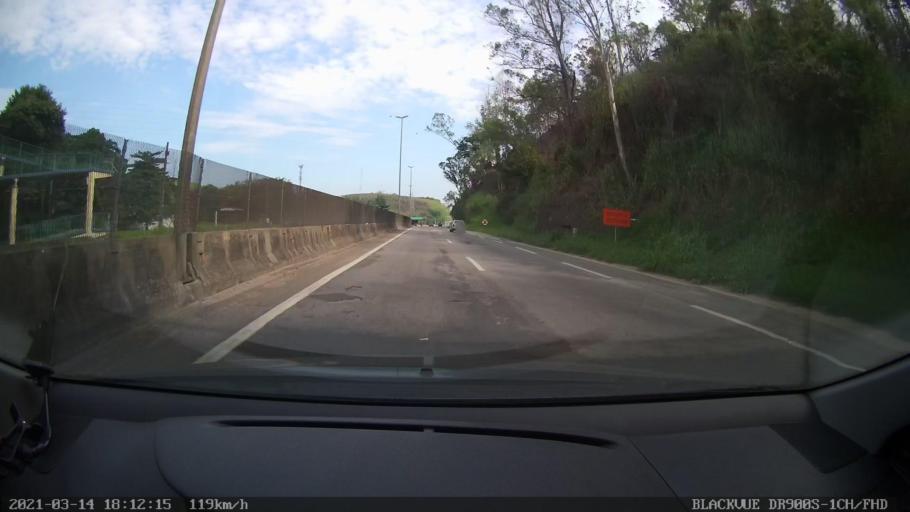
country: BR
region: Rio de Janeiro
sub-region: Duque De Caxias
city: Duque de Caxias
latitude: -22.6268
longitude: -43.2864
